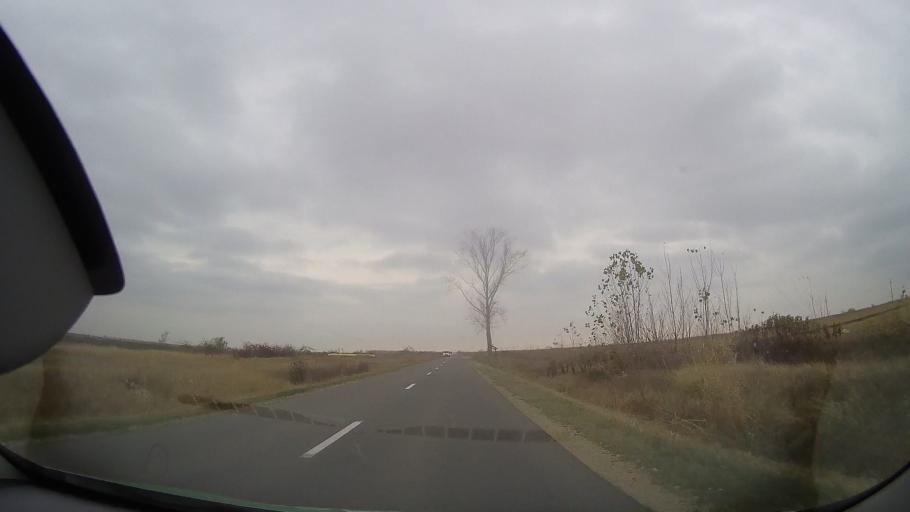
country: RO
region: Ialomita
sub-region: Comuna Garbovi
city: Garbovi
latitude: 44.7580
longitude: 26.7291
